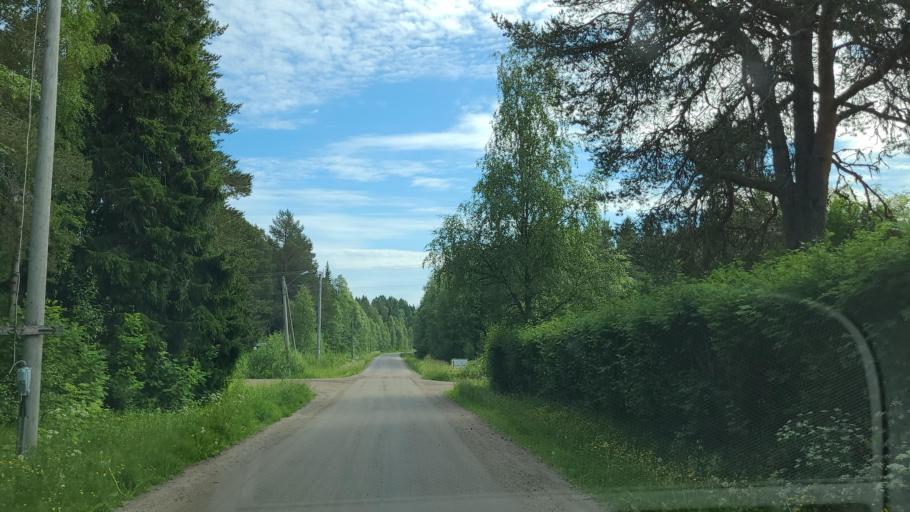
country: SE
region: Vaesterbotten
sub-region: Robertsfors Kommun
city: Robertsfors
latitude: 64.1624
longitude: 20.9653
